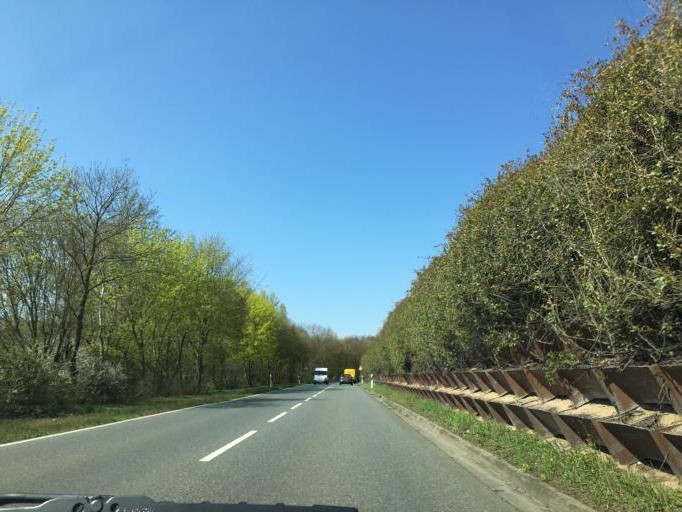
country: DE
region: Hesse
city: Obertshausen
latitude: 50.0713
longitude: 8.8677
